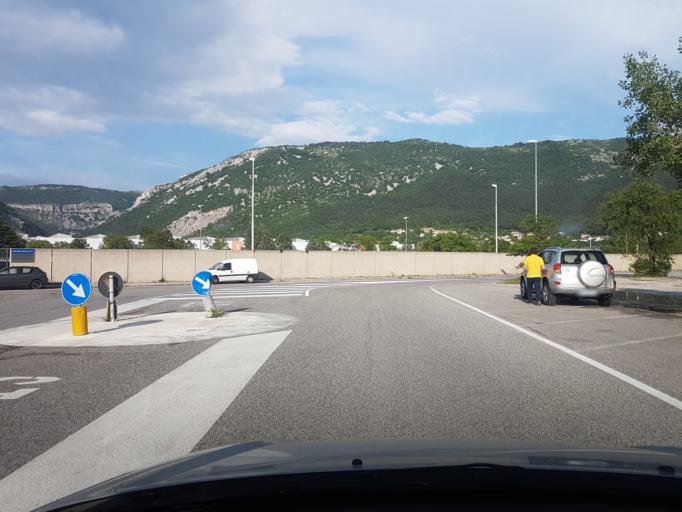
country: IT
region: Friuli Venezia Giulia
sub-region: Provincia di Trieste
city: Domio
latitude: 45.6091
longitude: 13.8455
